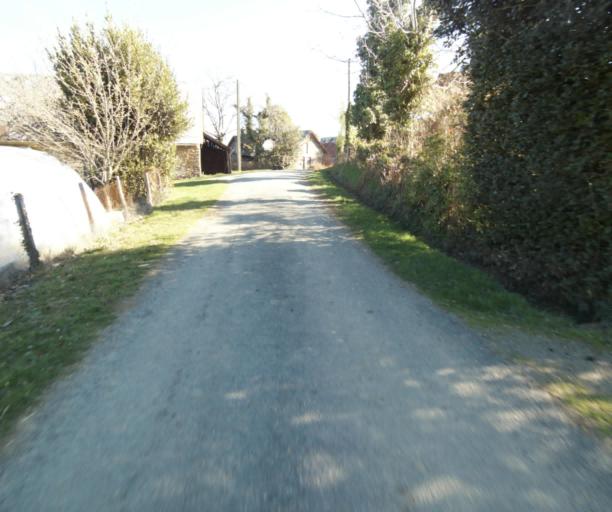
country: FR
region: Limousin
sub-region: Departement de la Correze
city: Saint-Clement
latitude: 45.3719
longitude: 1.6535
